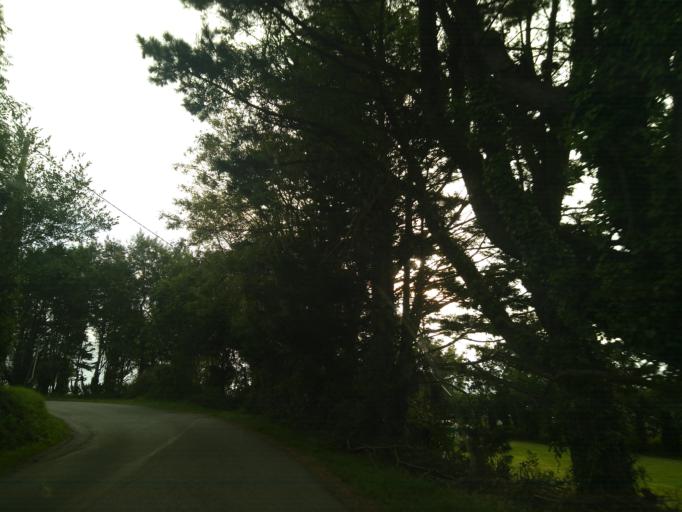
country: FR
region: Brittany
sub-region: Departement du Finistere
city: Crozon
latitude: 48.2390
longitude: -4.4562
